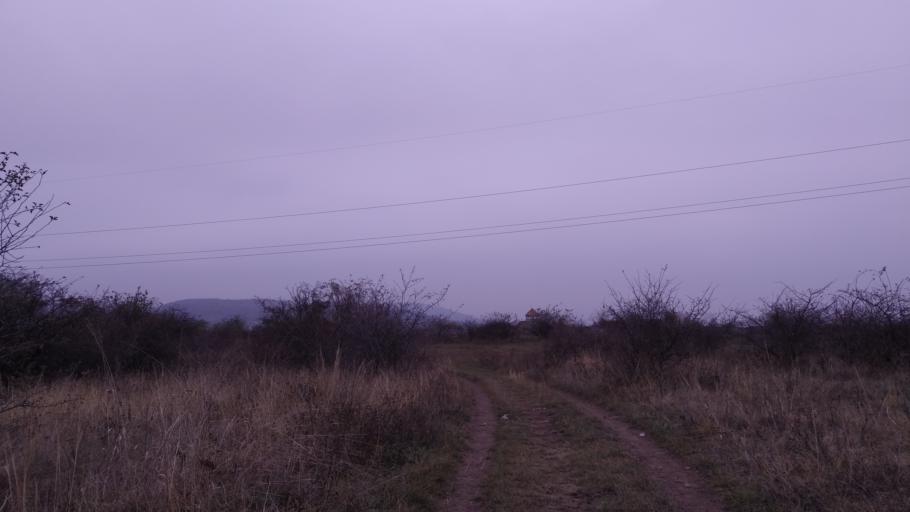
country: HU
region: Pest
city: Nagykovacsi
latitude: 47.6406
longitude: 19.0051
